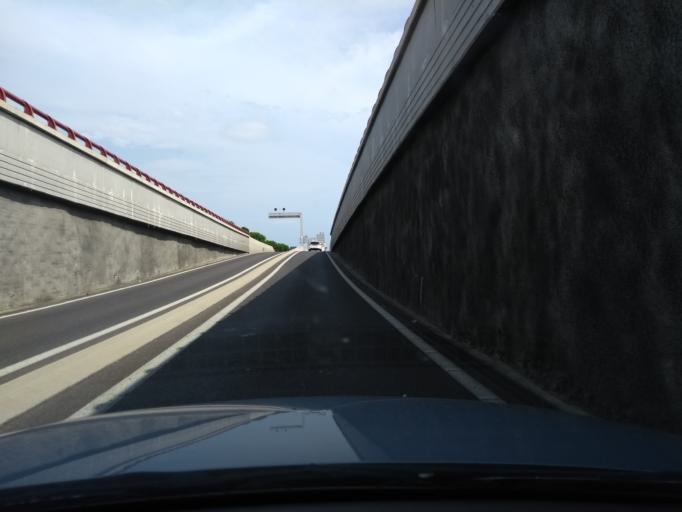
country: FR
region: Languedoc-Roussillon
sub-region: Departement des Pyrenees-Orientales
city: Perpignan
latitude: 42.6738
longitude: 2.8884
